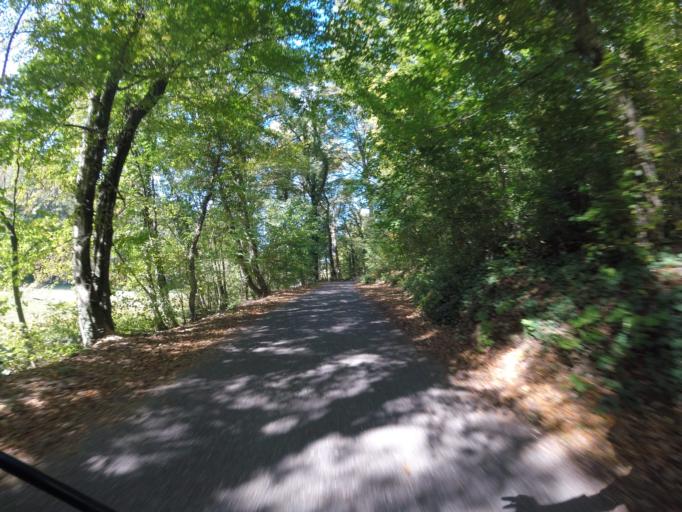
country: DE
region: Baden-Wuerttemberg
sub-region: Karlsruhe Region
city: Knittlingen
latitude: 49.0033
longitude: 8.7288
